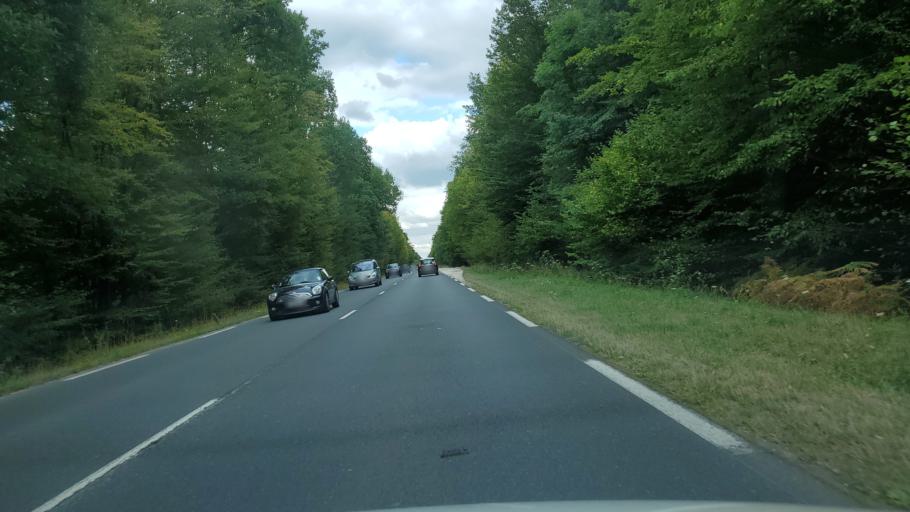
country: FR
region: Ile-de-France
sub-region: Departement de Seine-et-Marne
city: Villeneuve-le-Comte
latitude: 48.7998
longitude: 2.8534
